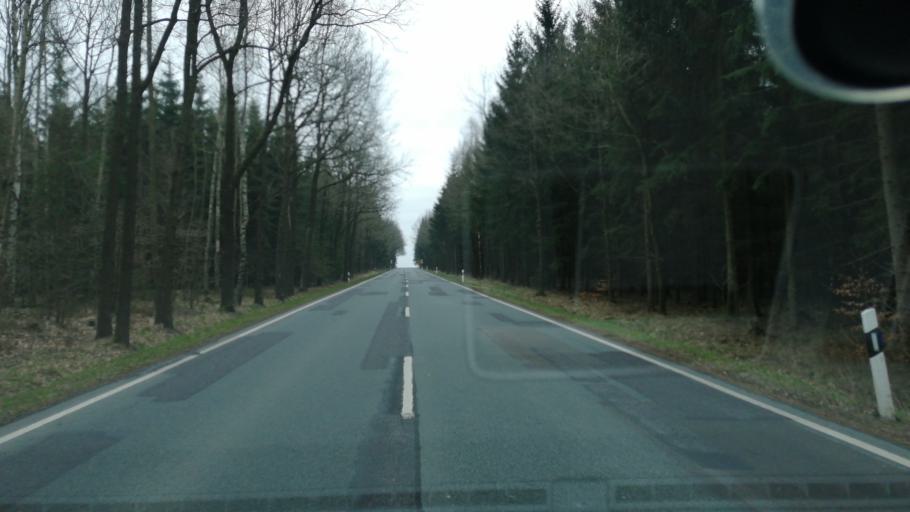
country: DE
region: Saxony
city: Niedercunnersdorf
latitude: 51.0495
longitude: 14.7024
